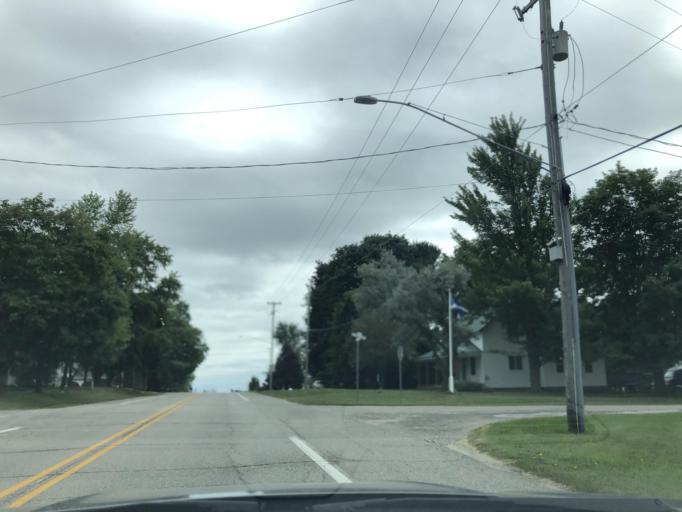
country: US
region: Michigan
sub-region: Missaukee County
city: Lake City
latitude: 44.1937
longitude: -85.2050
